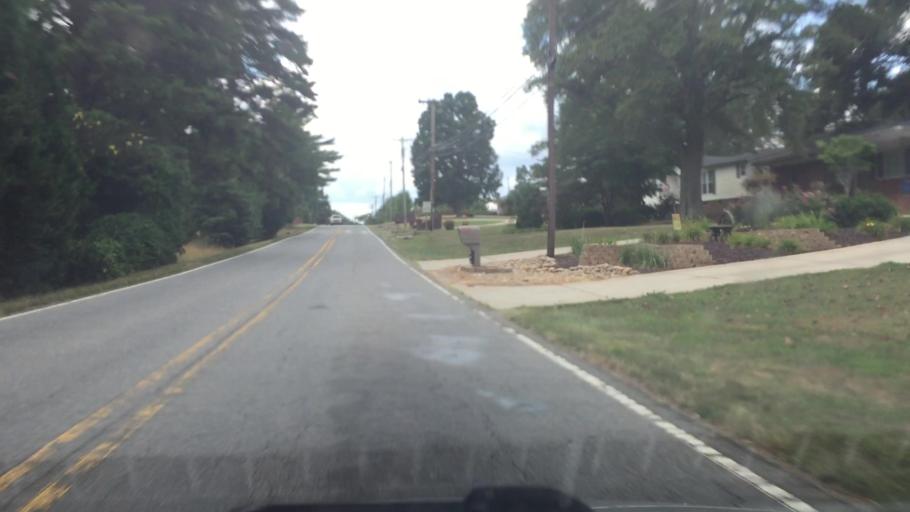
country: US
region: North Carolina
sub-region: Rowan County
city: Enochville
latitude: 35.5122
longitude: -80.6719
